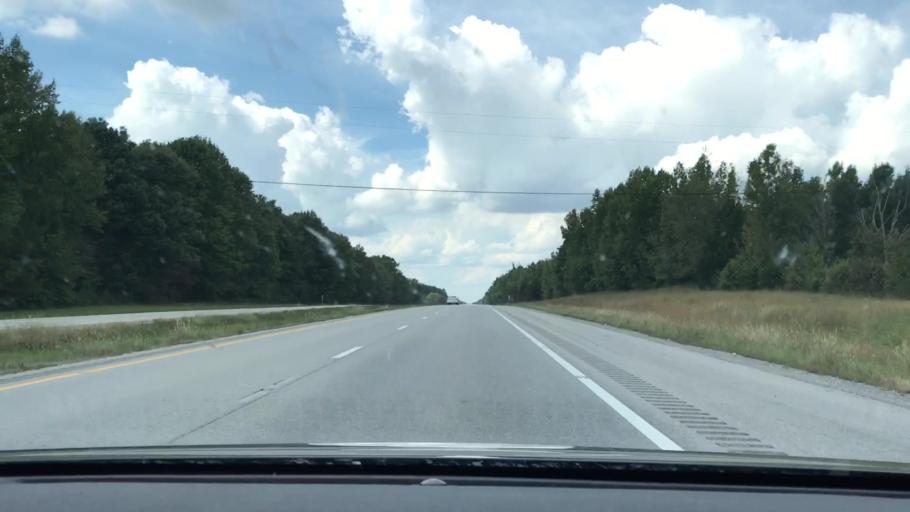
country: US
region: Kentucky
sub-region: Barren County
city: Glasgow
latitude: 37.0198
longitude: -86.0350
